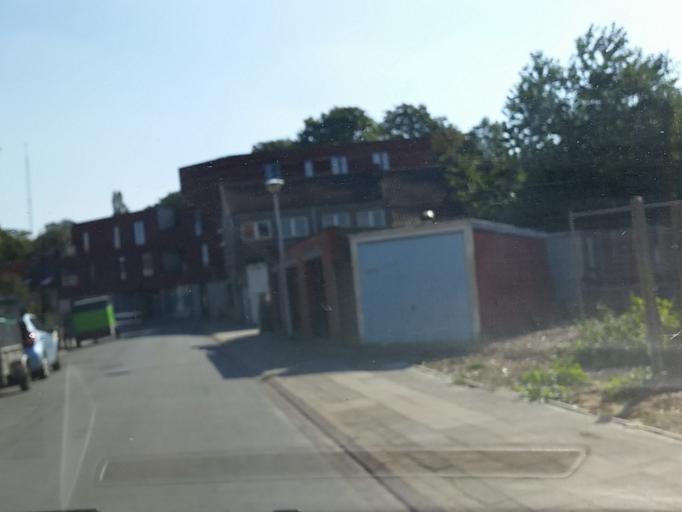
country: BE
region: Flanders
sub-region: Provincie Vlaams-Brabant
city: Machelen
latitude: 50.9268
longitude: 4.4577
